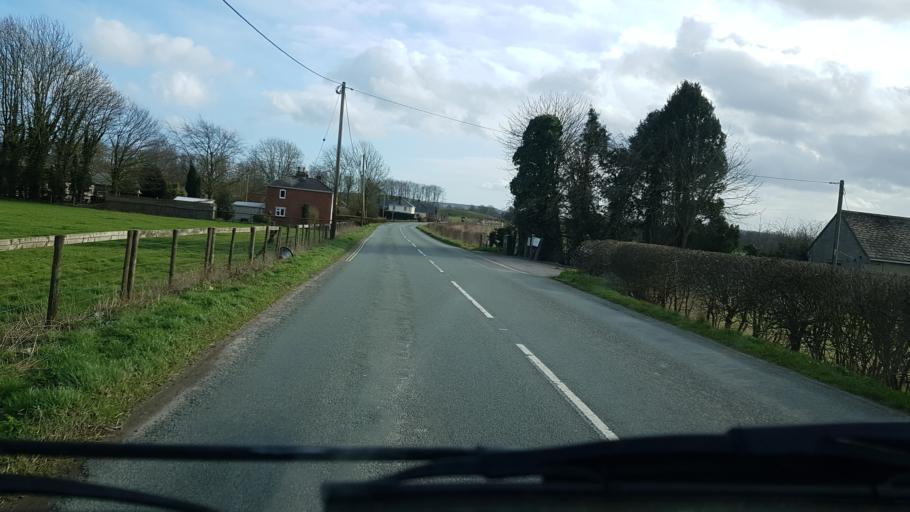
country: GB
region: England
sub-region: Wiltshire
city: Avebury
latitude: 51.4352
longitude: -1.8549
